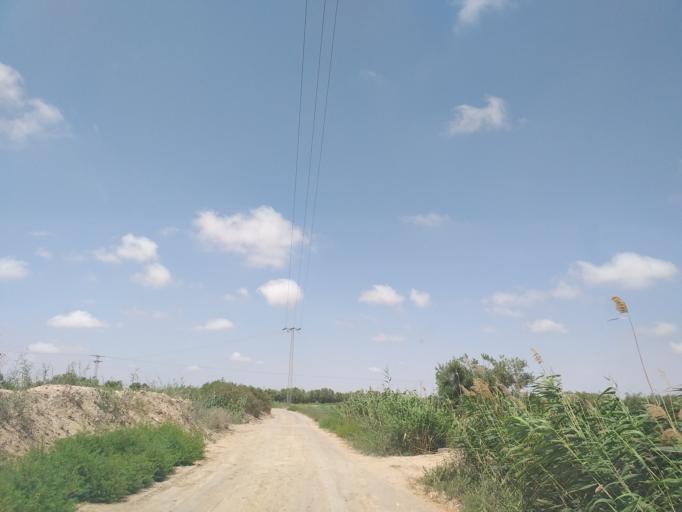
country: TN
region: Qabis
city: Gabes
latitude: 33.9523
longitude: 10.0430
